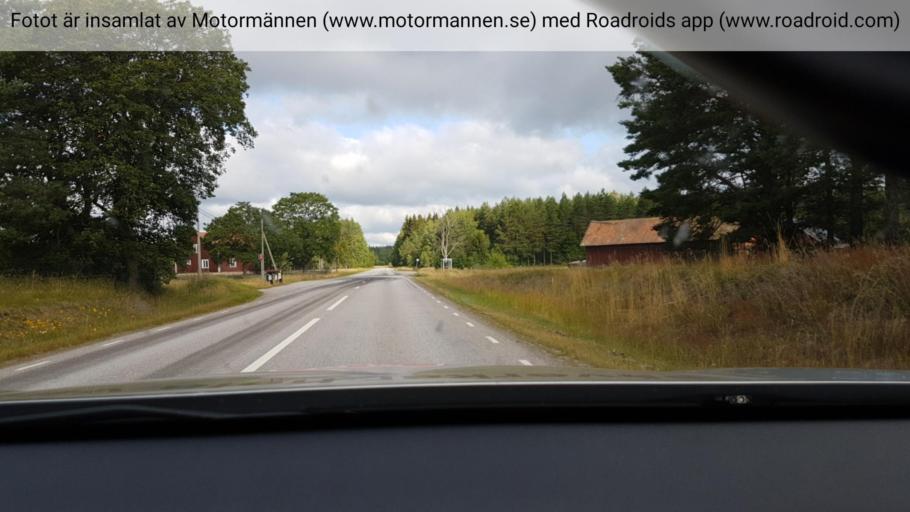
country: SE
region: Stockholm
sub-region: Norrtalje Kommun
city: Nykvarn
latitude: 59.9000
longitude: 18.3431
